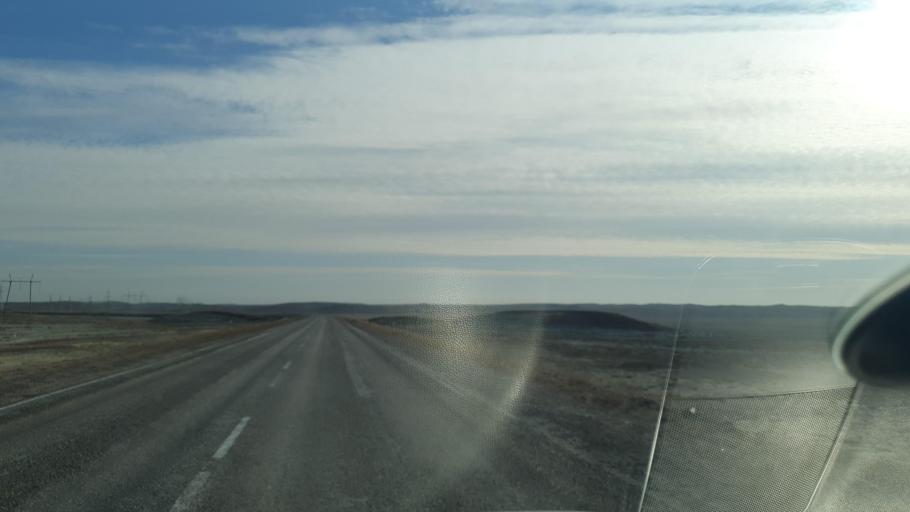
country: KZ
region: Zhambyl
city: Mynaral
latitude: 45.5687
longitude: 73.4184
